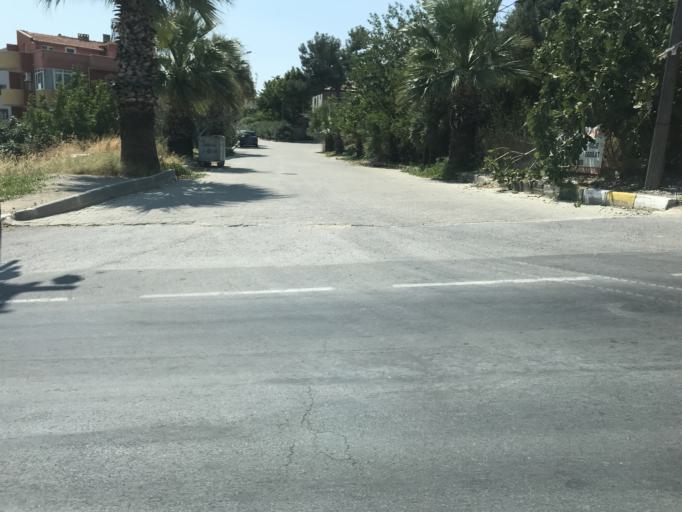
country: TR
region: Izmir
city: Urla
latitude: 38.3283
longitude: 26.7606
